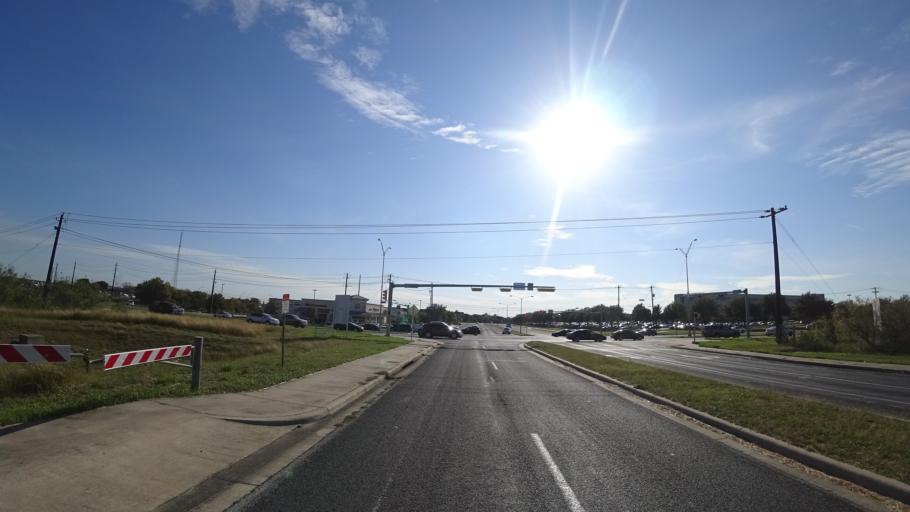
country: US
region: Texas
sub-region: Travis County
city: Wells Branch
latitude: 30.4026
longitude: -97.6570
